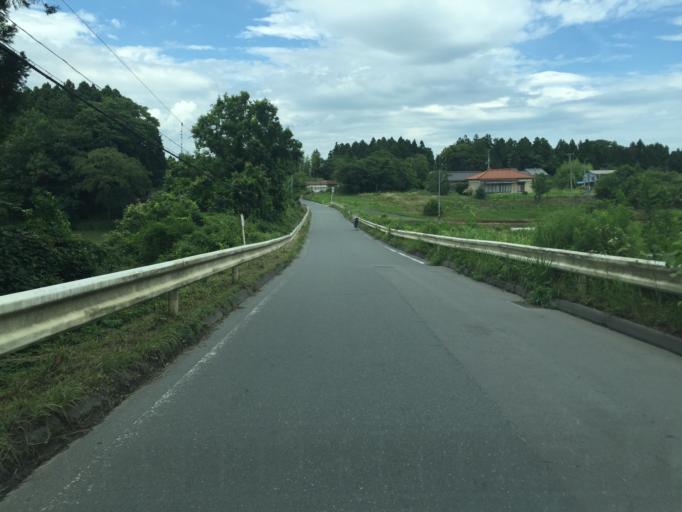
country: JP
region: Miyagi
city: Marumori
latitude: 37.7630
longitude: 140.9158
